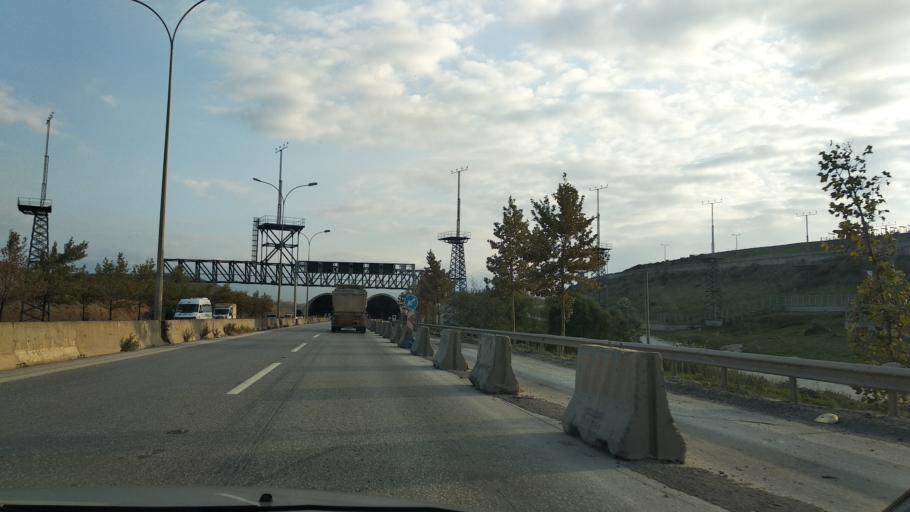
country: TR
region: Istanbul
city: Pendik
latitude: 40.9063
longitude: 29.3275
